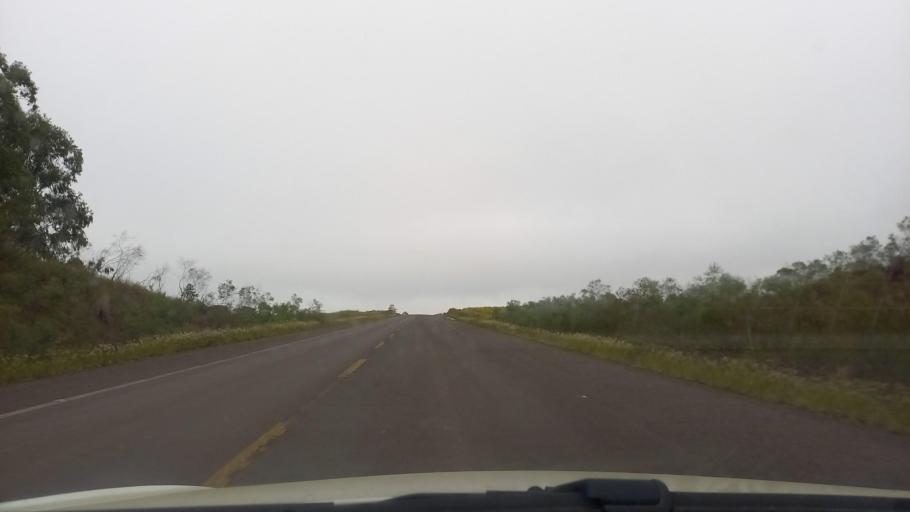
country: BR
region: Rio Grande do Sul
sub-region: Cacequi
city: Cacequi
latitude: -30.0445
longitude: -54.5953
